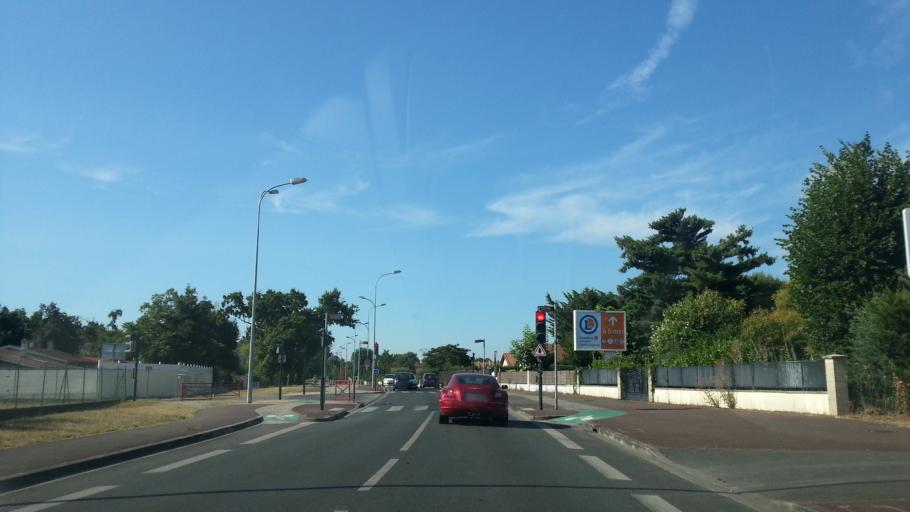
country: FR
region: Aquitaine
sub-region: Departement de la Gironde
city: Leognan
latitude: 44.7622
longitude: -0.5817
